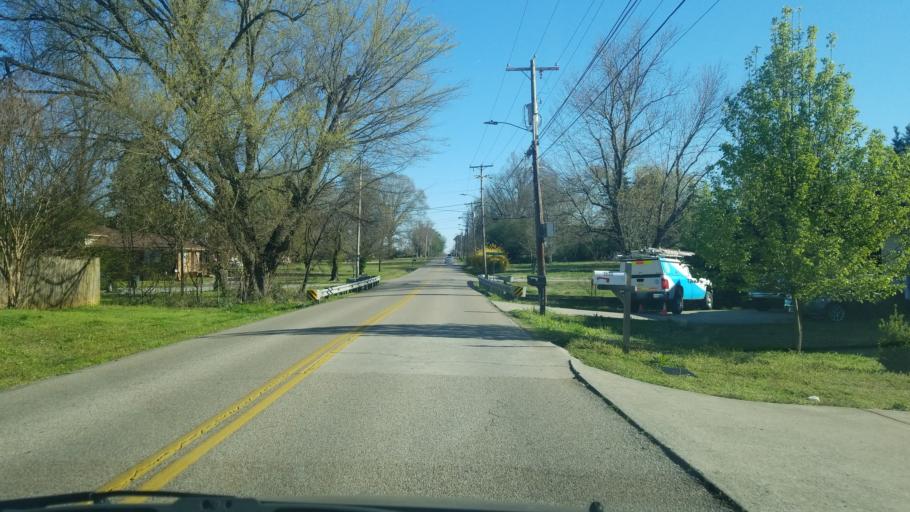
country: US
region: Tennessee
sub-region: Hamilton County
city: East Brainerd
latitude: 35.0352
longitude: -85.1722
